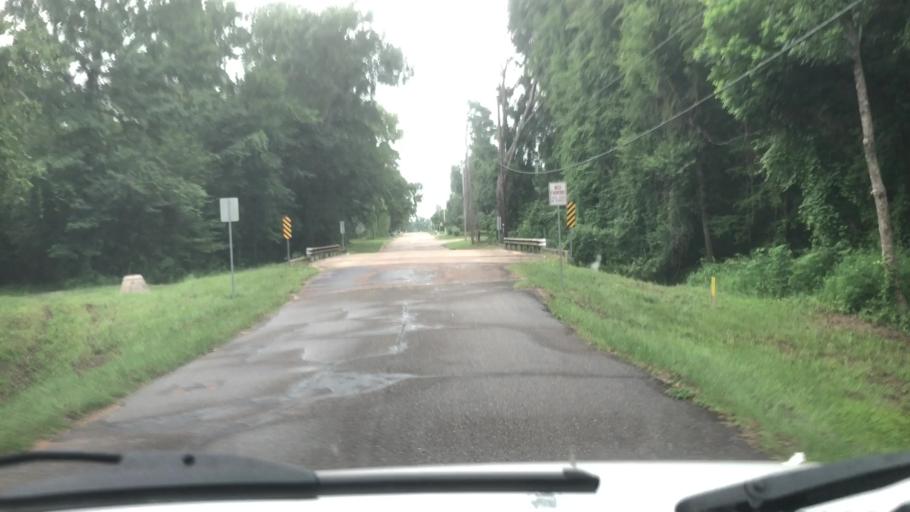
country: US
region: Texas
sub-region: Bowie County
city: Wake Village
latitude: 33.3983
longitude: -94.0832
